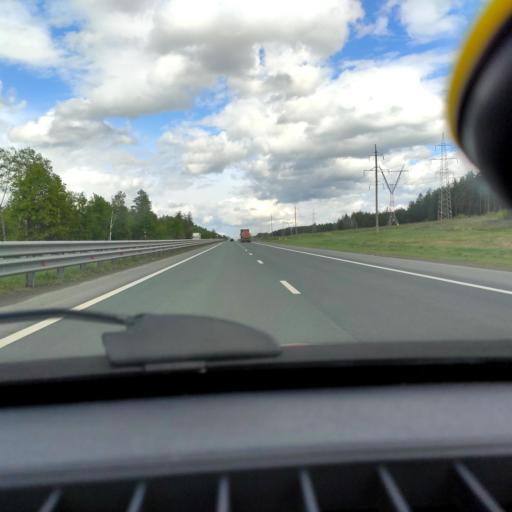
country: RU
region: Samara
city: Povolzhskiy
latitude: 53.5158
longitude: 49.7108
